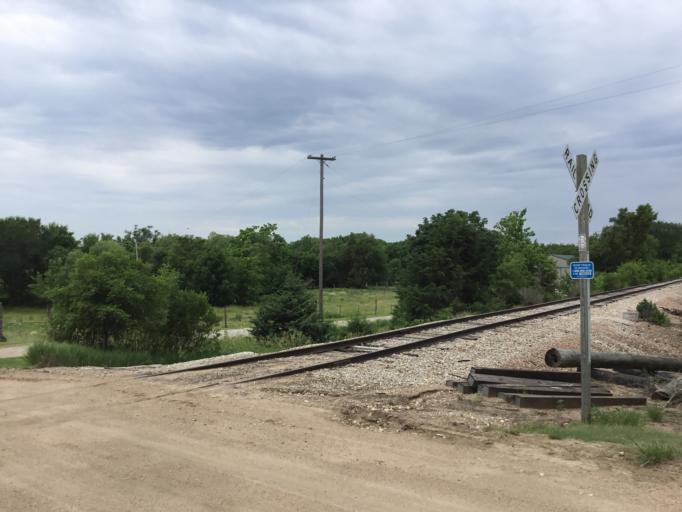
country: US
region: Kansas
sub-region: Republic County
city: Belleville
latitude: 39.8265
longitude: -97.6406
